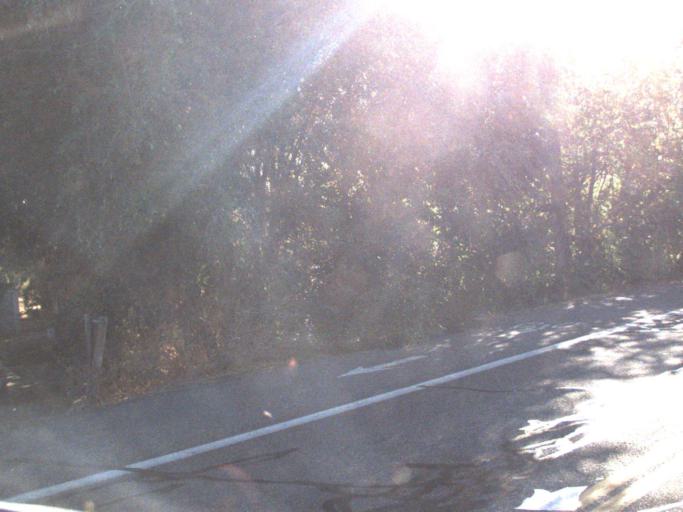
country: US
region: Washington
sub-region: Benton County
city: Benton City
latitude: 46.2737
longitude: -119.4918
